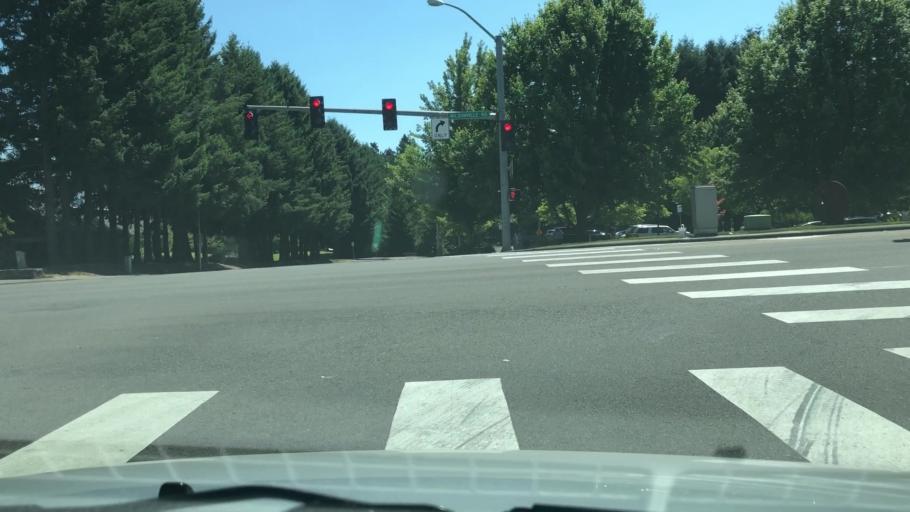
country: US
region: Oregon
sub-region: Clackamas County
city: Wilsonville
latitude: 45.3031
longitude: -122.7604
